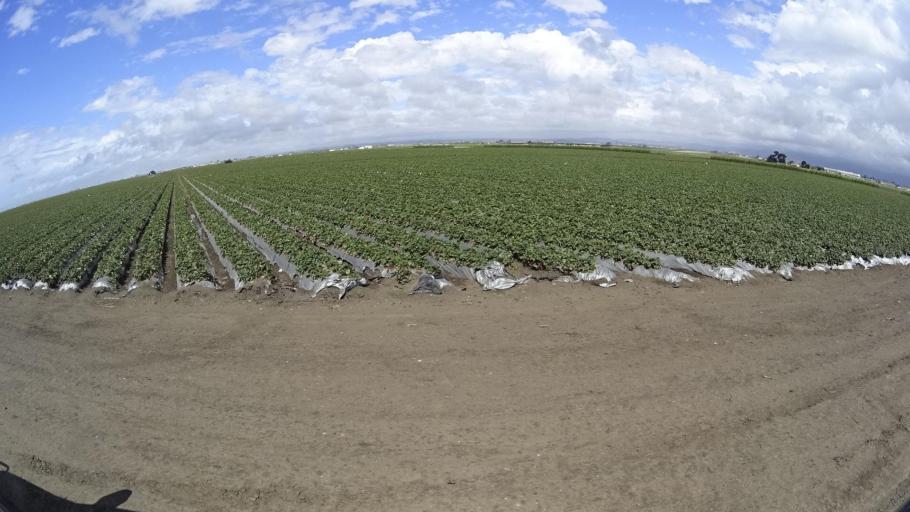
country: US
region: California
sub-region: Monterey County
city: Boronda
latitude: 36.6920
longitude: -121.7098
